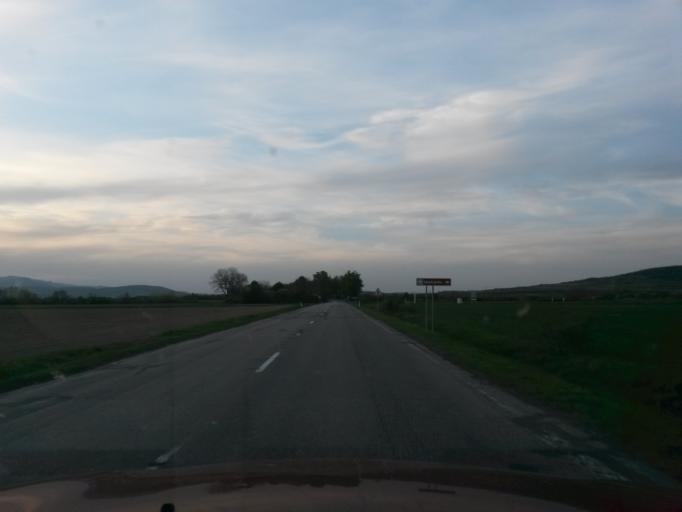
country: HU
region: Borsod-Abauj-Zemplen
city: Satoraljaujhely
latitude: 48.4434
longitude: 21.6539
